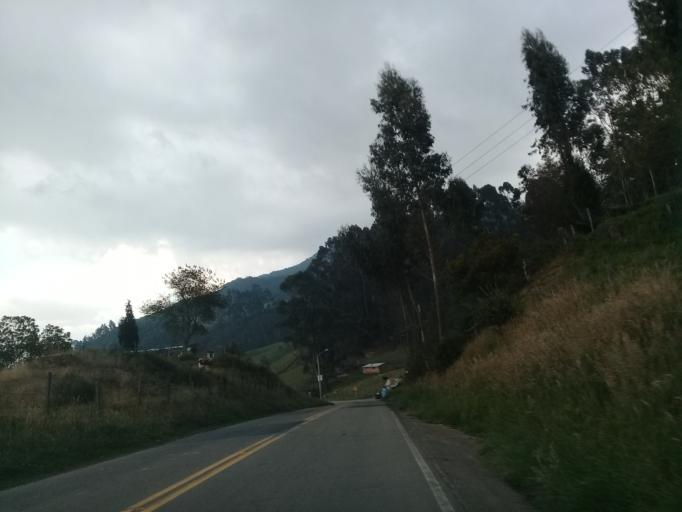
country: CO
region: Cundinamarca
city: Zipaquira
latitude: 5.0574
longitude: -74.0556
